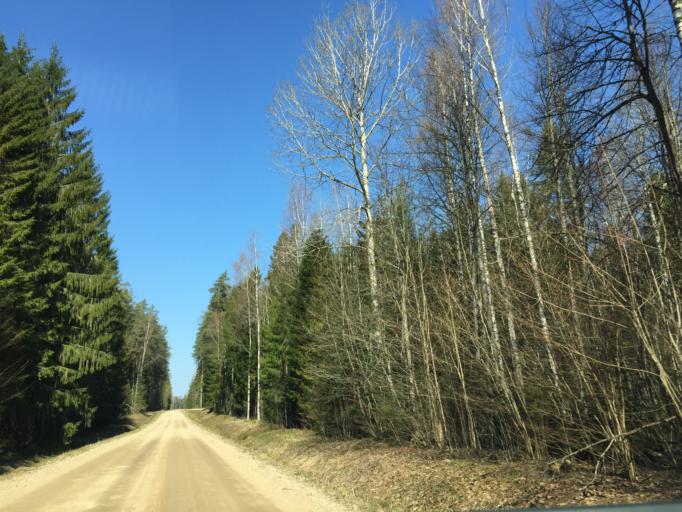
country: EE
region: Tartu
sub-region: Alatskivi vald
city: Kallaste
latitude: 58.5512
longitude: 26.9342
